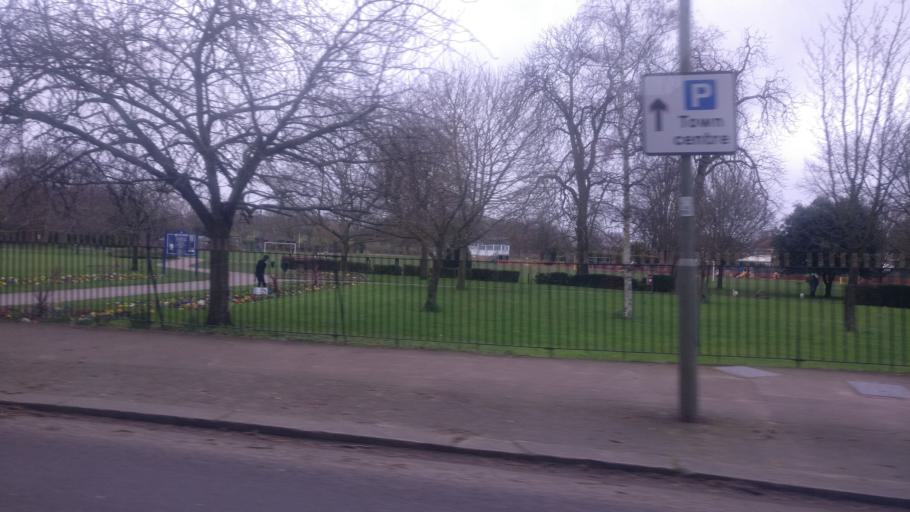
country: GB
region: England
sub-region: Surrey
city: Addlestone
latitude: 51.3747
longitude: -0.4931
